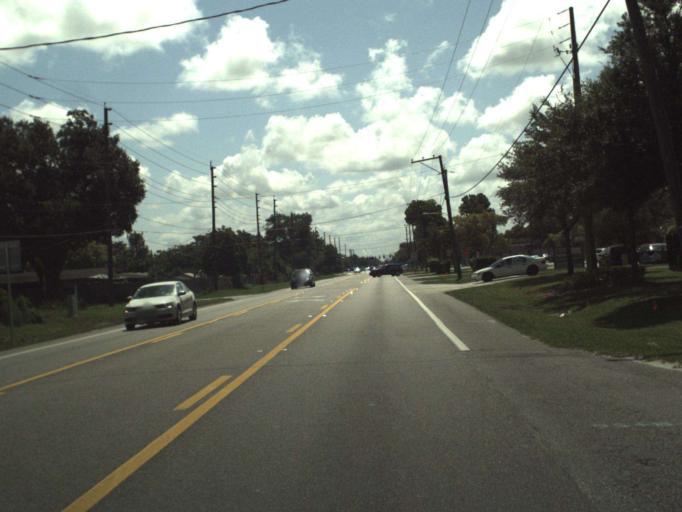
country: US
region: Florida
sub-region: Orange County
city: Conway
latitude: 28.4806
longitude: -81.3149
